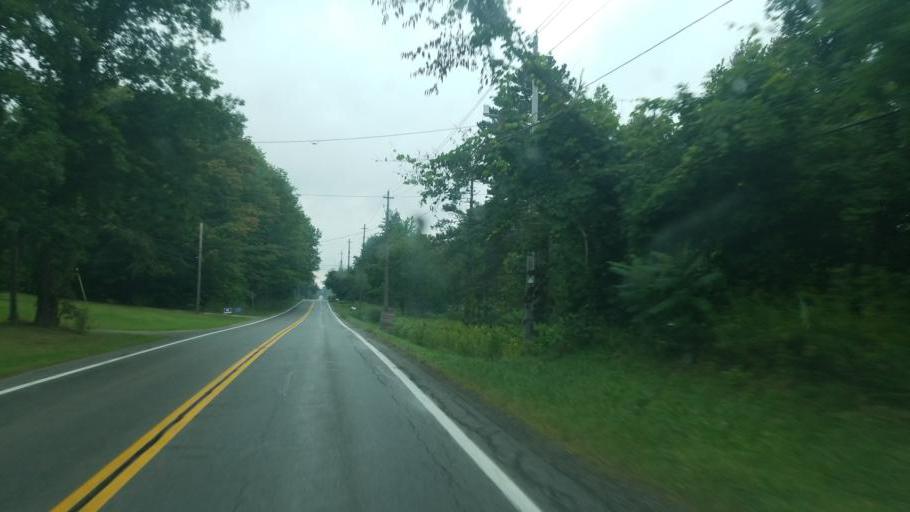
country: US
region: Ohio
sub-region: Geauga County
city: Burton
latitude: 41.4850
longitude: -81.1936
